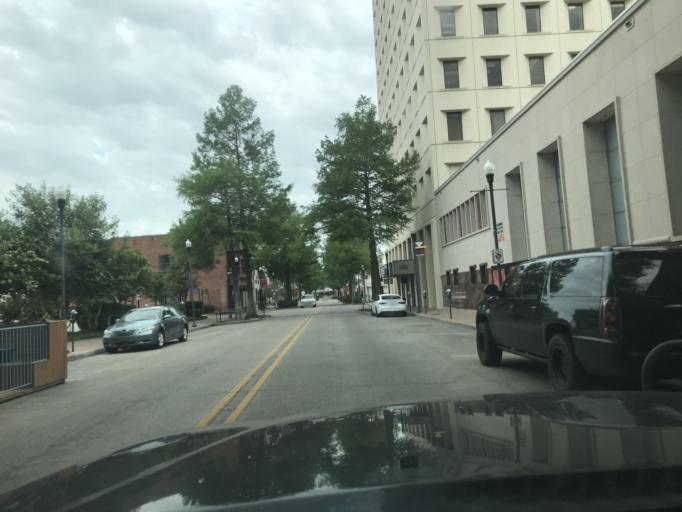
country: US
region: Louisiana
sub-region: Lafayette Parish
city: Lafayette
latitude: 30.2239
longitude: -92.0188
